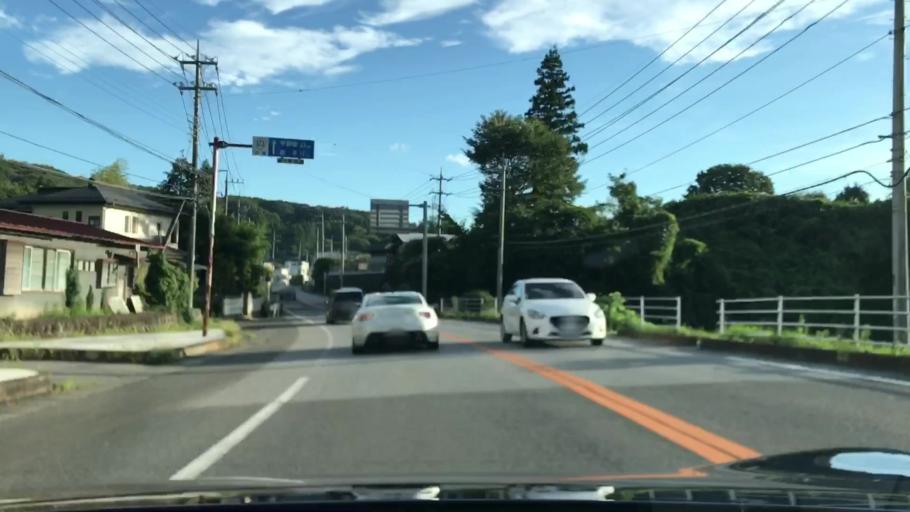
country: JP
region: Tochigi
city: Motegi
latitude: 36.5365
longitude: 140.2063
